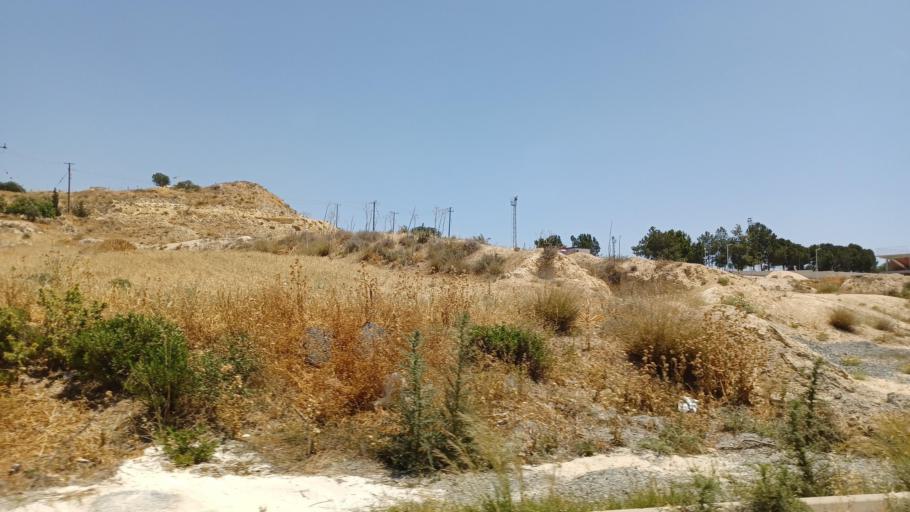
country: CY
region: Larnaka
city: Pyla
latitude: 34.9999
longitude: 33.6921
